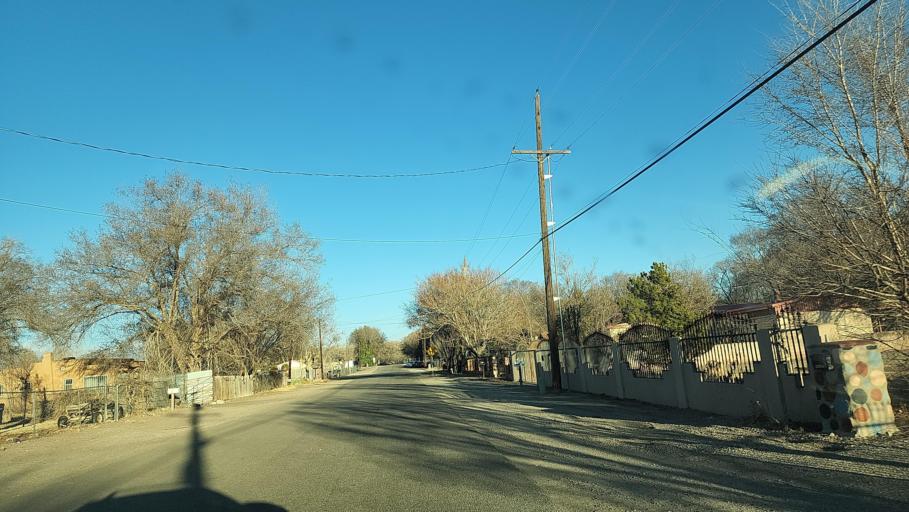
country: US
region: New Mexico
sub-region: Bernalillo County
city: South Valley
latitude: 35.0307
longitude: -106.6777
